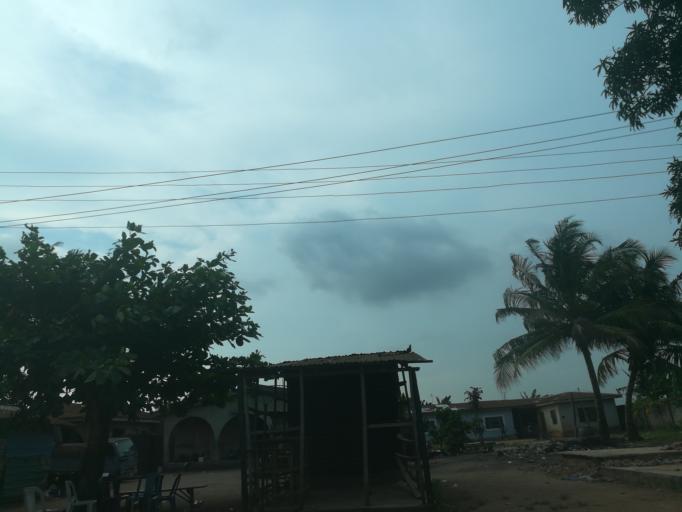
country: NG
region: Lagos
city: Ikorodu
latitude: 6.6118
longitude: 3.5972
